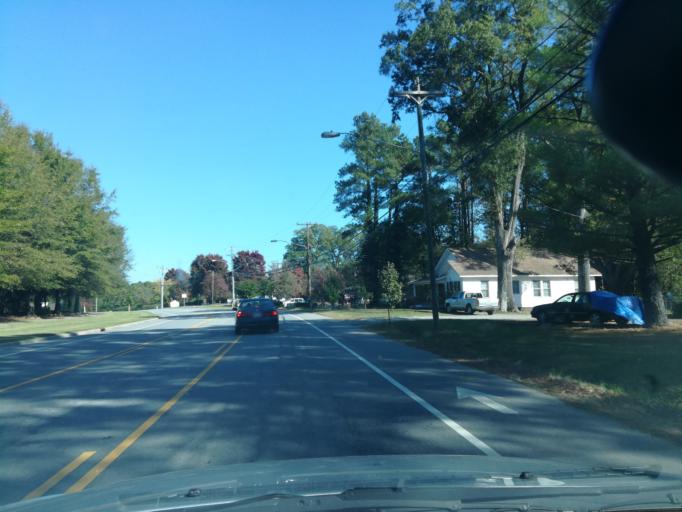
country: US
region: North Carolina
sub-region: Durham County
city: Durham
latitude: 36.0300
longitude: -78.9115
